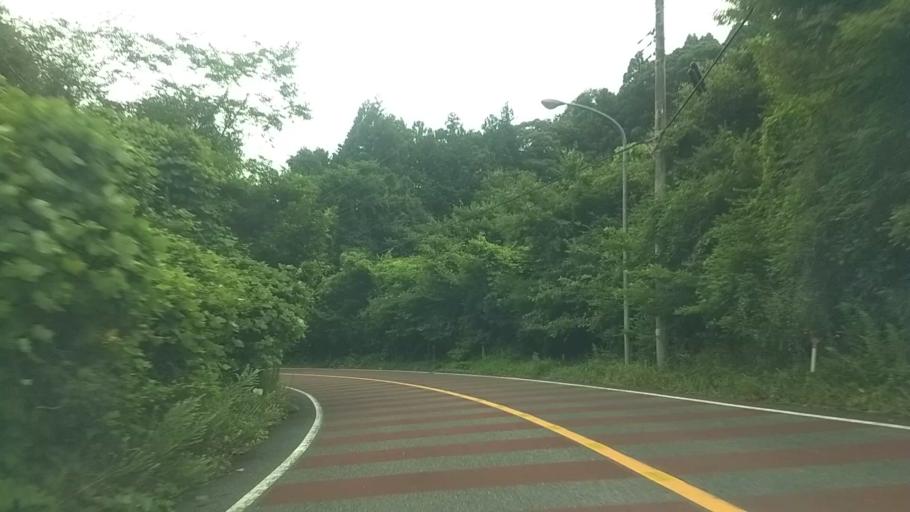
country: JP
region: Chiba
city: Kawaguchi
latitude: 35.2228
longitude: 140.0715
